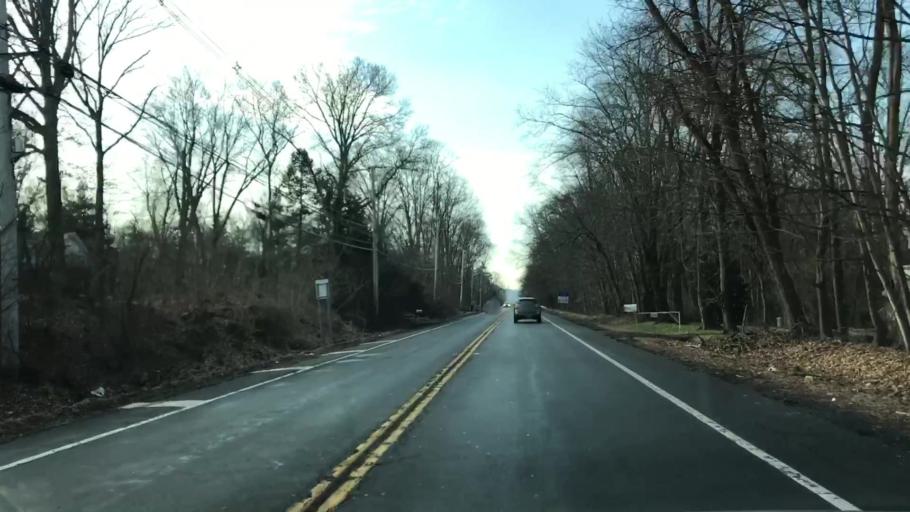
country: US
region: New York
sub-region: Rockland County
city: Congers
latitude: 41.1380
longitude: -73.9375
